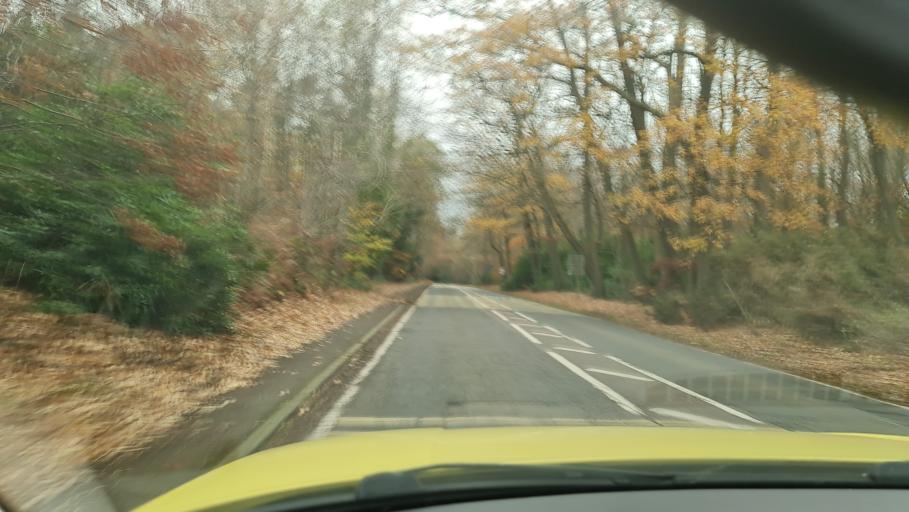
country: GB
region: England
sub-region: Bracknell Forest
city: Sandhurst
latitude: 51.3190
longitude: -0.7804
